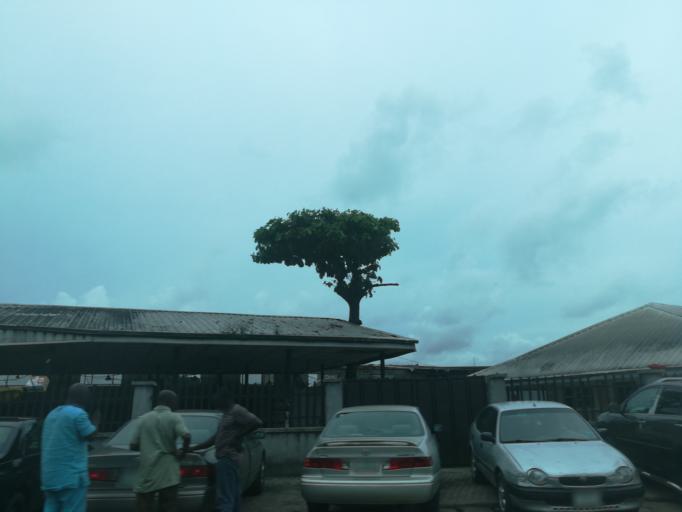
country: NG
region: Rivers
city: Port Harcourt
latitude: 4.8213
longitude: 7.0005
